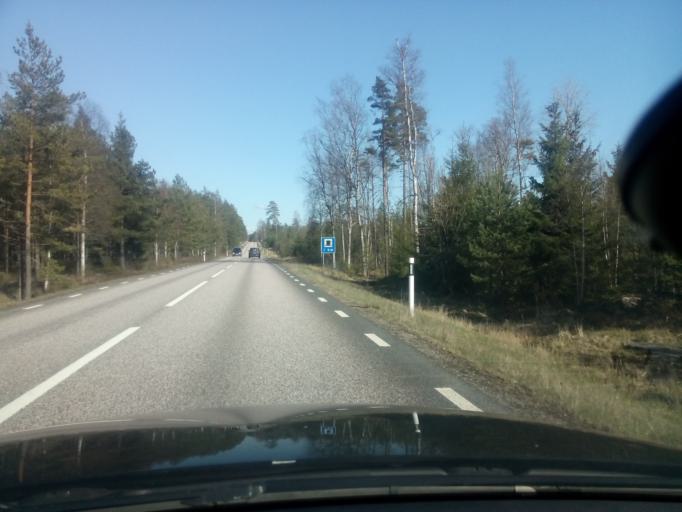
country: SE
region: Soedermanland
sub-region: Flens Kommun
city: Malmkoping
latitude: 59.2060
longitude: 16.8047
